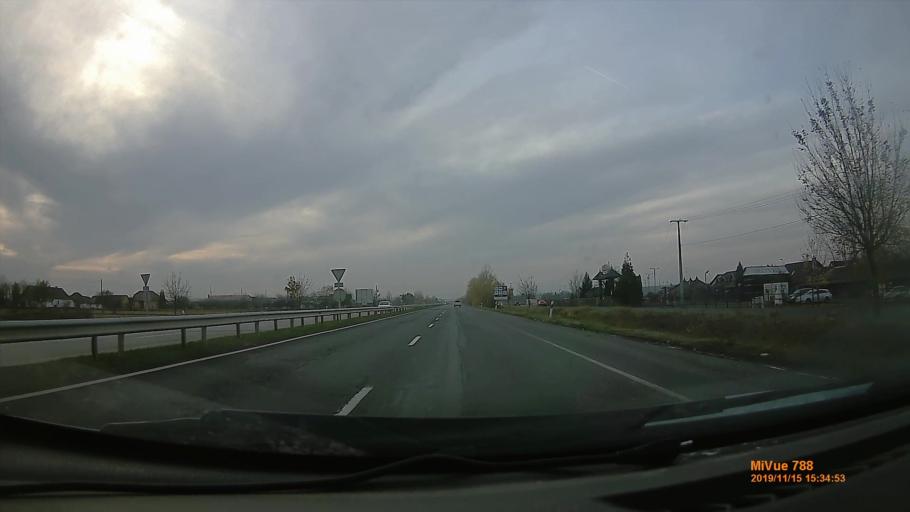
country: HU
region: Bekes
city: Gyula
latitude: 46.6532
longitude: 21.2364
